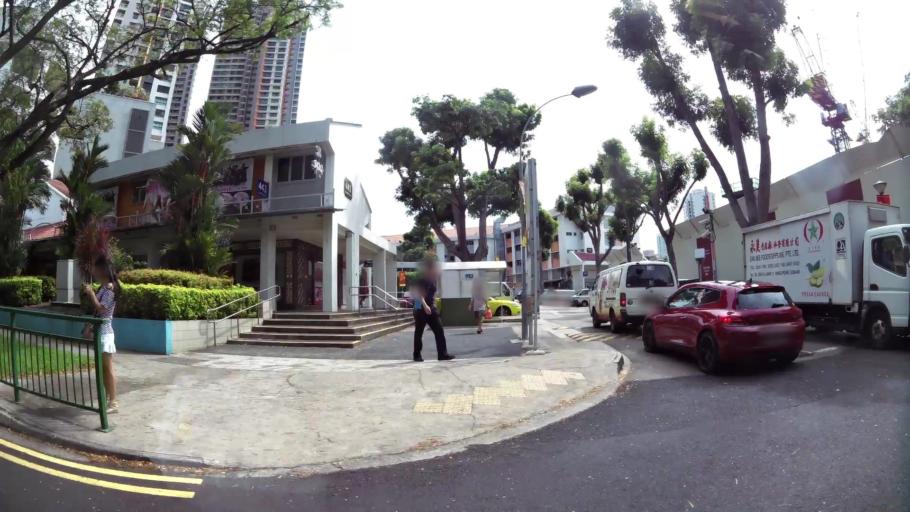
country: SG
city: Singapore
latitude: 1.3134
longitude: 103.7638
